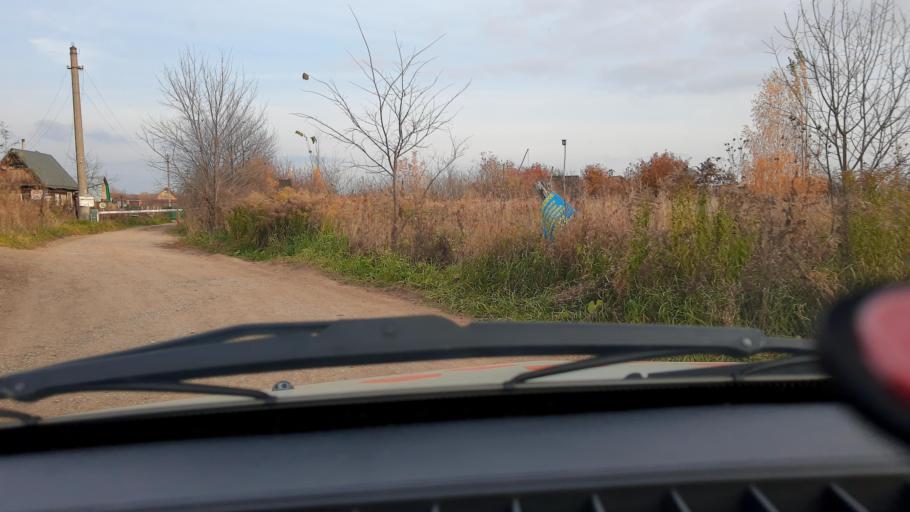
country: RU
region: Bashkortostan
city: Iglino
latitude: 54.7971
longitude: 56.3454
